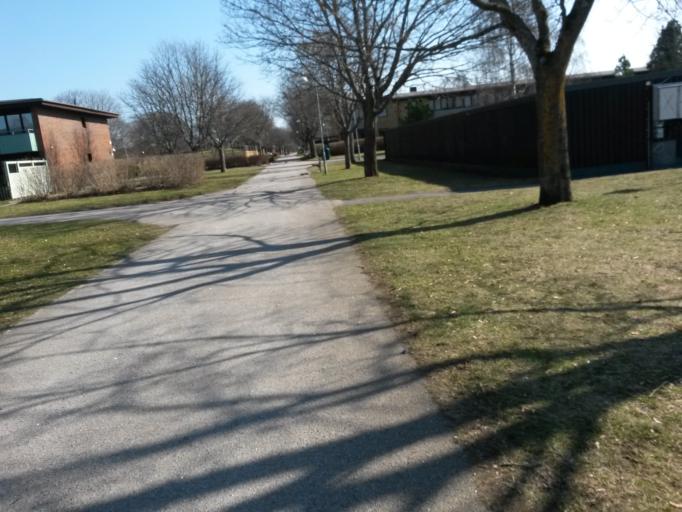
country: SE
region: Vaestra Goetaland
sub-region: Vargarda Kommun
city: Vargarda
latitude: 58.0355
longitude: 12.7999
